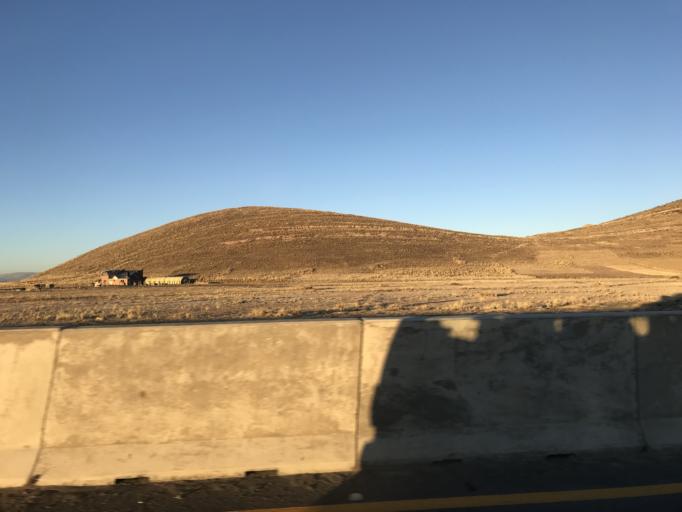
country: BO
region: La Paz
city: Batallas
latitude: -16.3037
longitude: -68.4813
